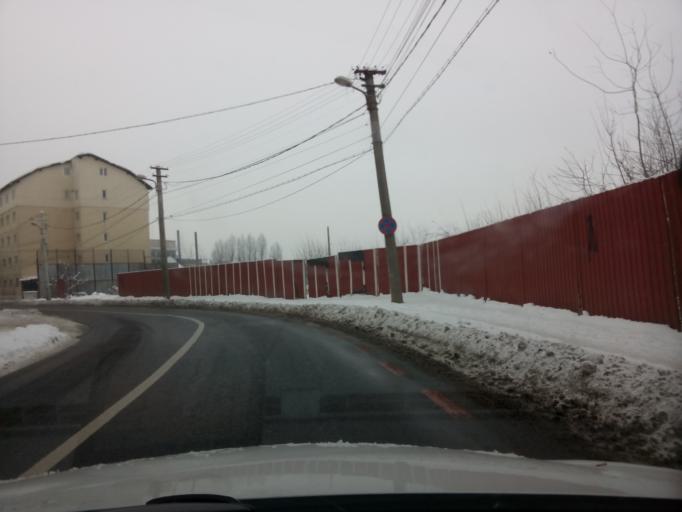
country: RO
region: Sibiu
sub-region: Municipiul Sibiu
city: Sibiu
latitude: 45.8034
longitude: 24.1561
